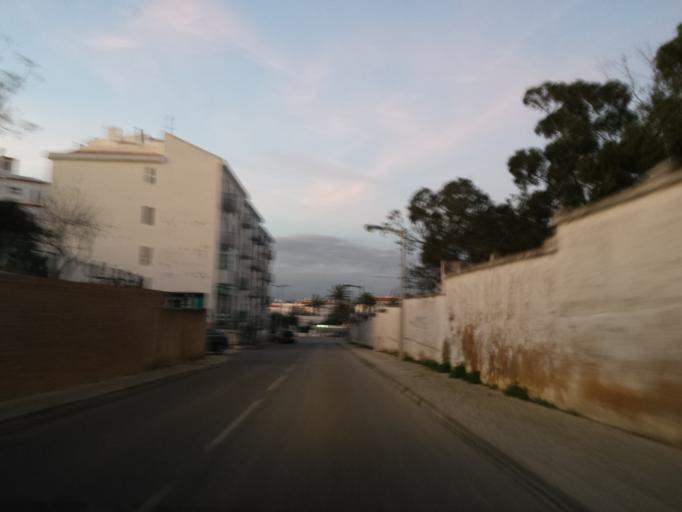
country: PT
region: Faro
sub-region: Lagos
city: Lagos
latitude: 37.0936
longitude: -8.6721
